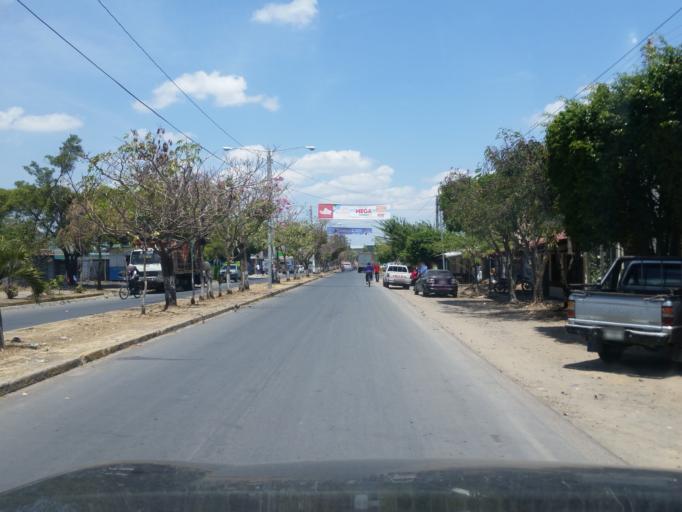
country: NI
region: Esteli
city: Esteli
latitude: 13.0786
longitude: -86.3552
